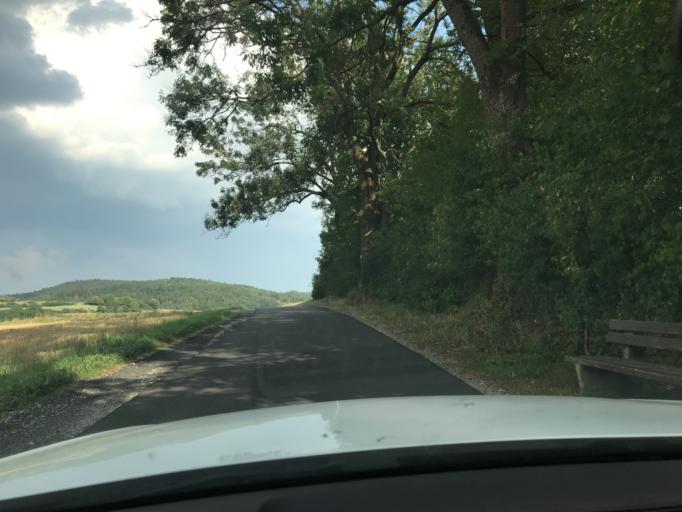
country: DE
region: Bavaria
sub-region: Upper Franconia
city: Pegnitz
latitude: 49.7504
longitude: 11.5503
